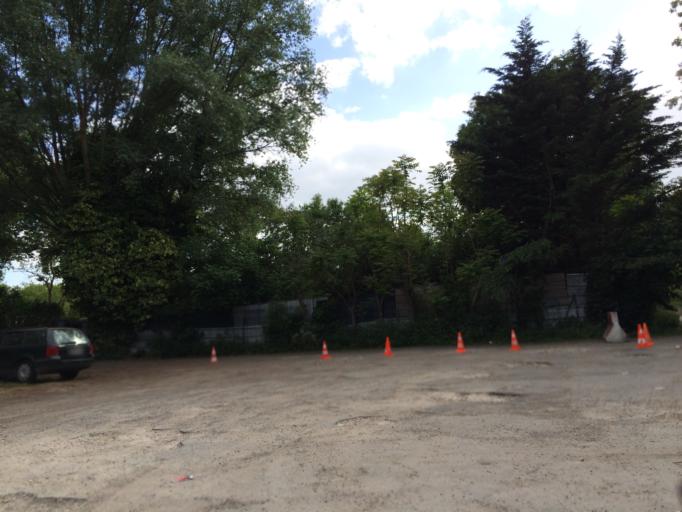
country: FR
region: Ile-de-France
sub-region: Departement de l'Essonne
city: Viry-Chatillon
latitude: 48.6711
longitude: 2.4067
